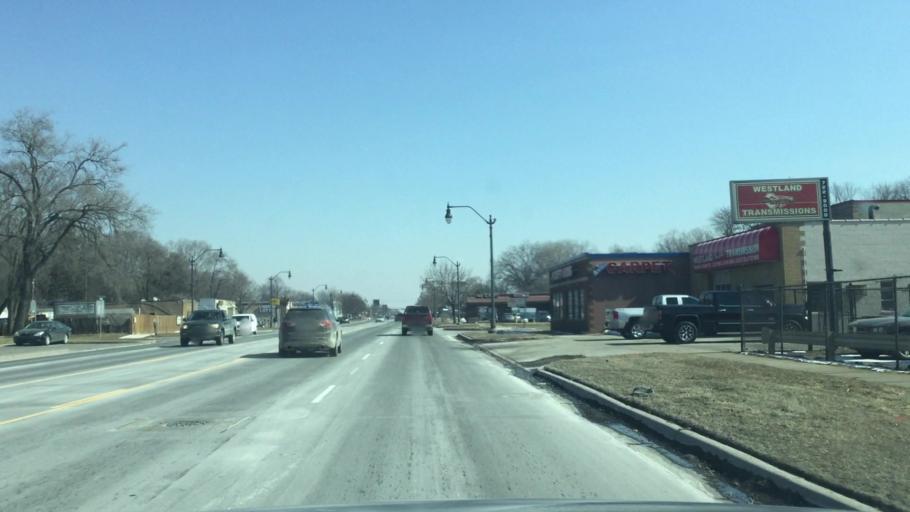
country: US
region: Michigan
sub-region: Wayne County
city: Westland
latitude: 42.3242
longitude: -83.3971
